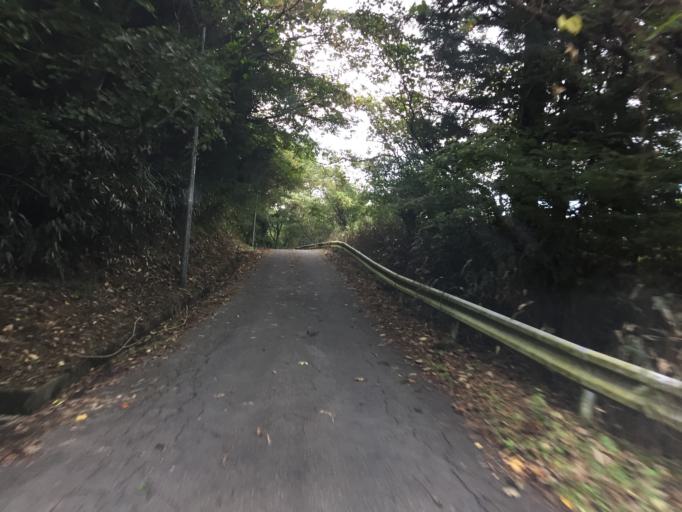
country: JP
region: Miyagi
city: Marumori
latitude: 37.9338
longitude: 140.7108
